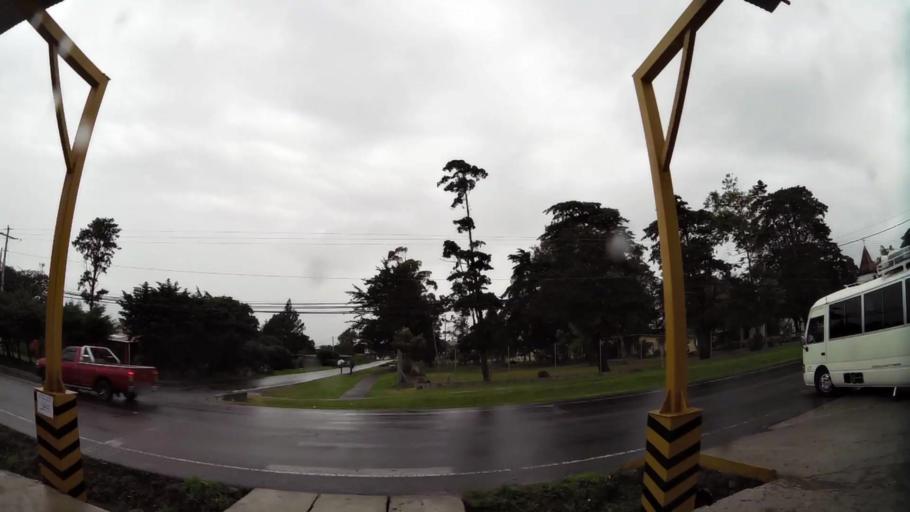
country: PA
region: Chiriqui
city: Volcan
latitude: 8.7773
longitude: -82.6399
